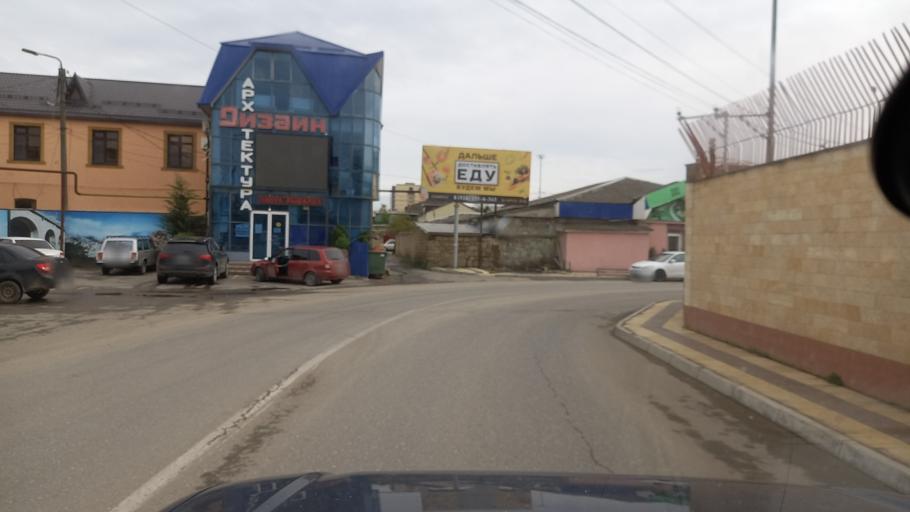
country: RU
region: Dagestan
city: Derbent
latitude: 42.0617
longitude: 48.3040
